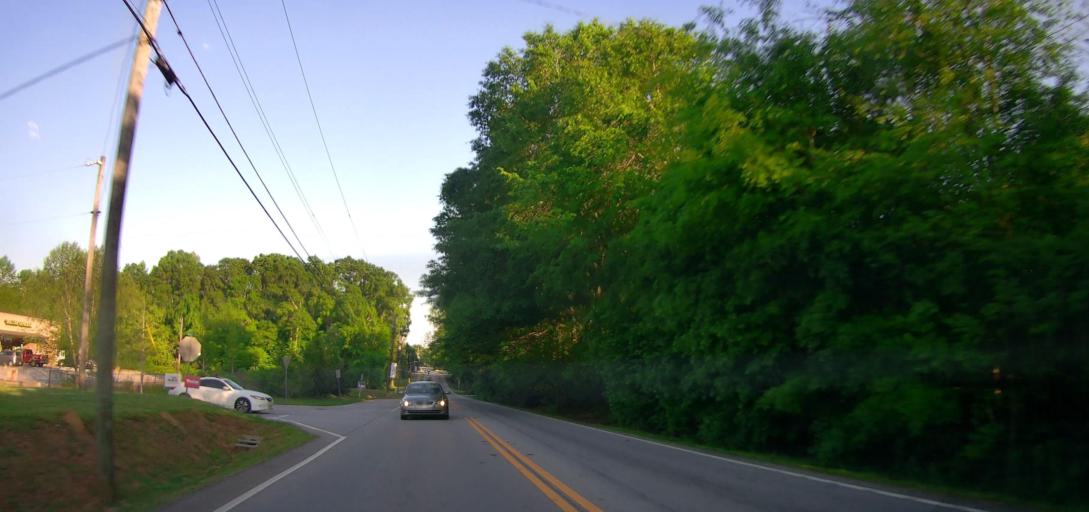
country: US
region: Georgia
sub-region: Walton County
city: Social Circle
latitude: 33.5198
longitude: -83.6991
